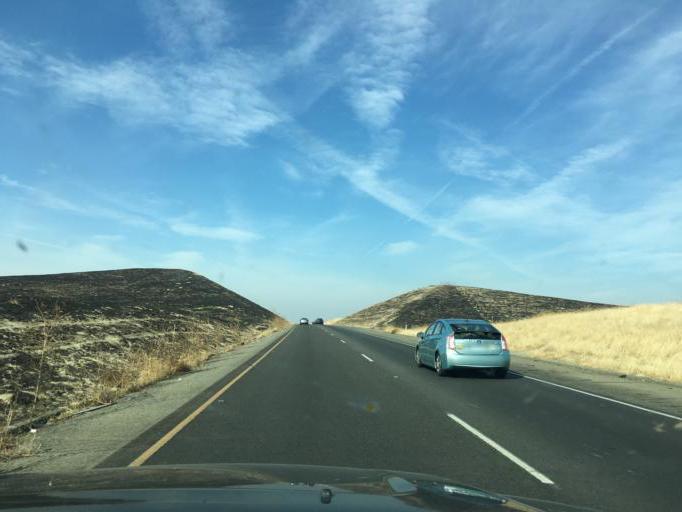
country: US
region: California
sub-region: Fresno County
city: Coalinga
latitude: 36.3194
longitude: -120.2894
